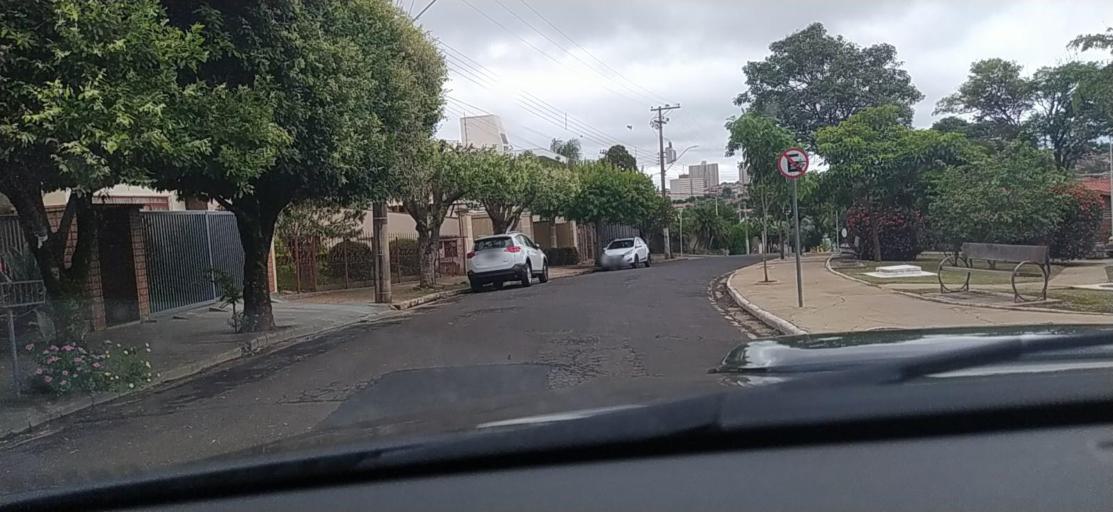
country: BR
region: Sao Paulo
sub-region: Olimpia
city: Olimpia
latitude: -20.7333
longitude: -48.9157
